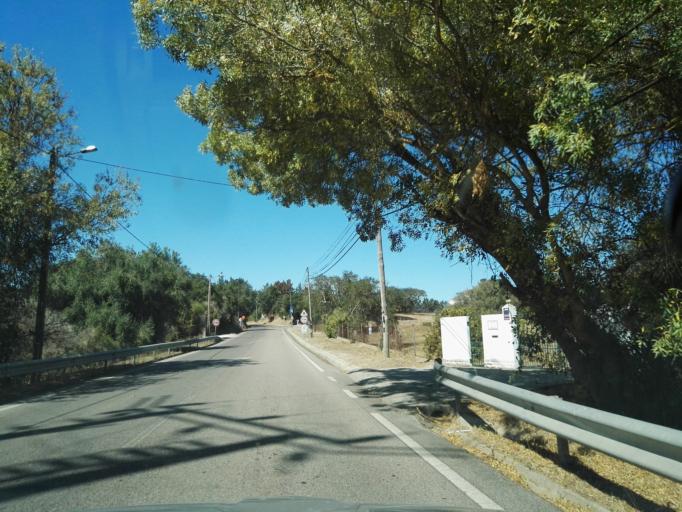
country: PT
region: Santarem
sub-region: Benavente
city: Poceirao
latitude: 38.8564
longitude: -8.7321
